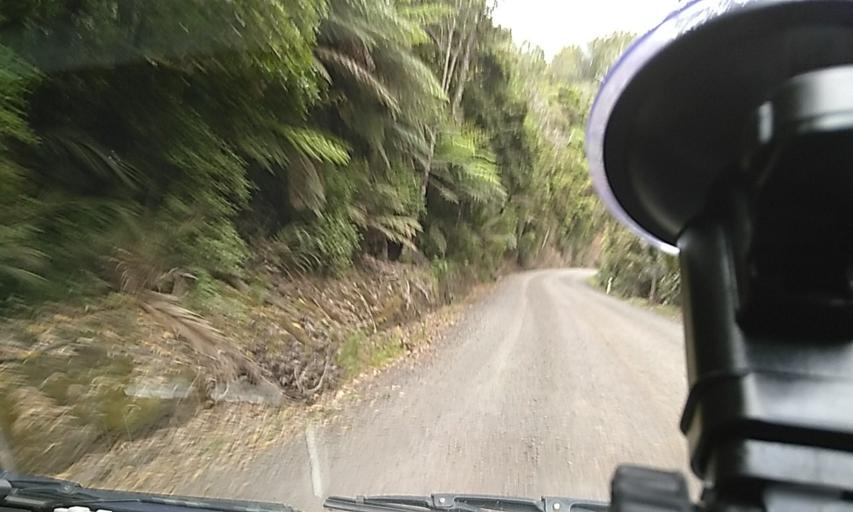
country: NZ
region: Northland
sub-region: Kaipara District
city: Dargaville
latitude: -35.6521
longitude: 173.5645
